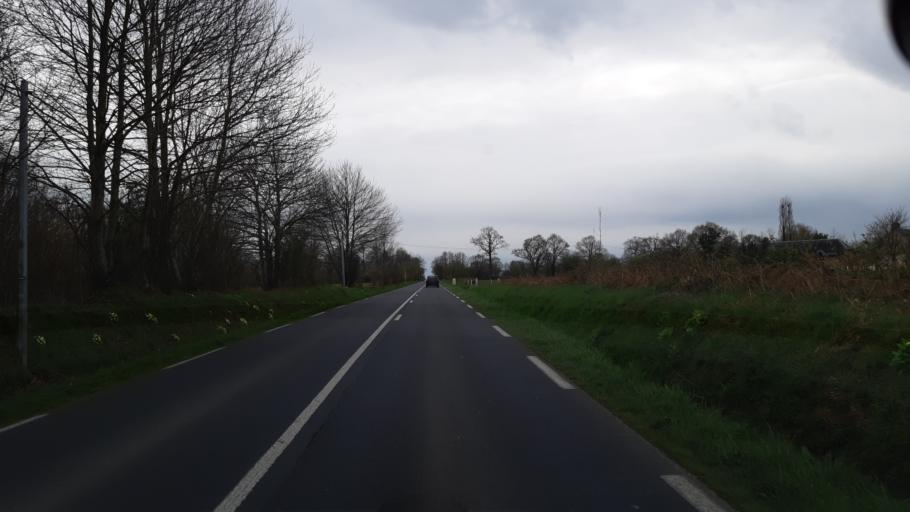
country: FR
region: Lower Normandy
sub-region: Departement de la Manche
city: Tessy-sur-Vire
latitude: 49.0204
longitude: -1.1470
